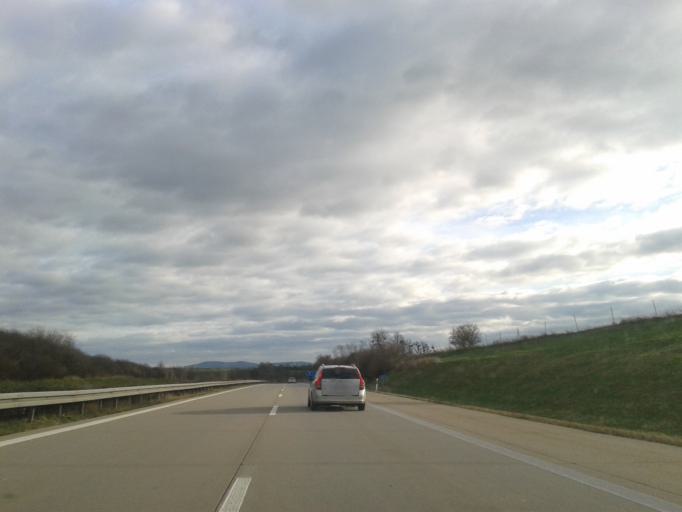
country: DE
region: Saxony
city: Weissenberg
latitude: 51.2081
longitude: 14.6412
